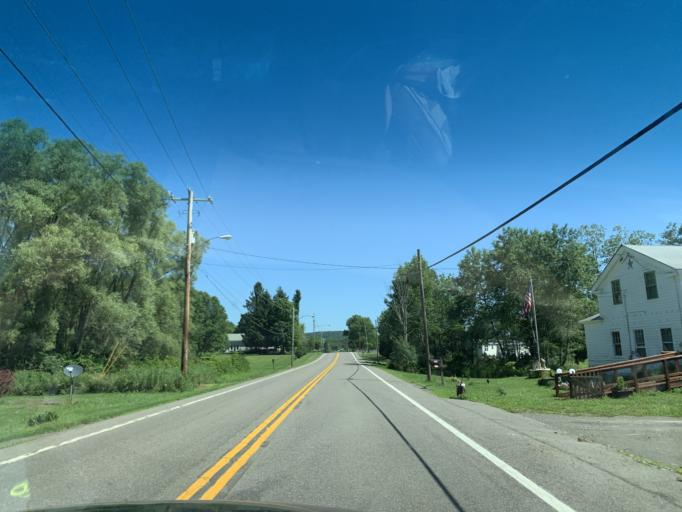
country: US
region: New York
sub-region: Chenango County
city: Norwich
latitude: 42.5148
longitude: -75.4007
